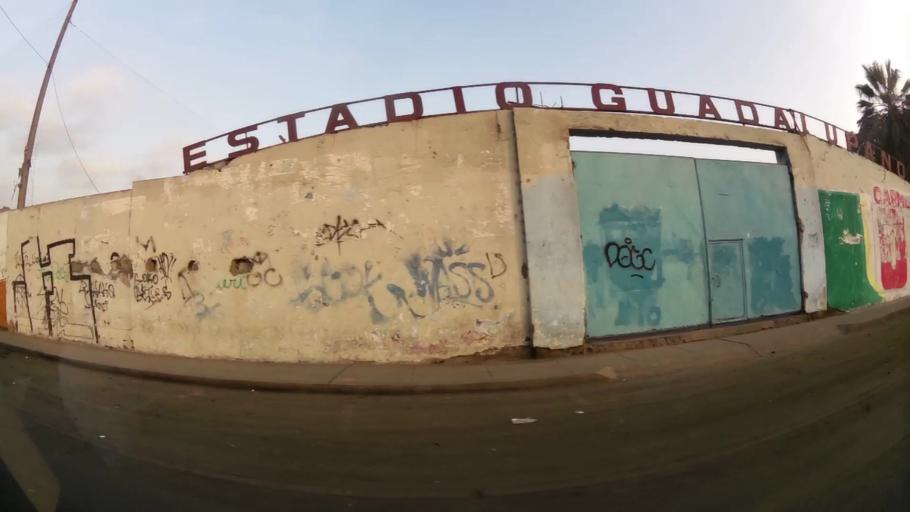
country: PE
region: Lima
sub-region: Lima
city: Independencia
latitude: -12.0051
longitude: -77.0646
